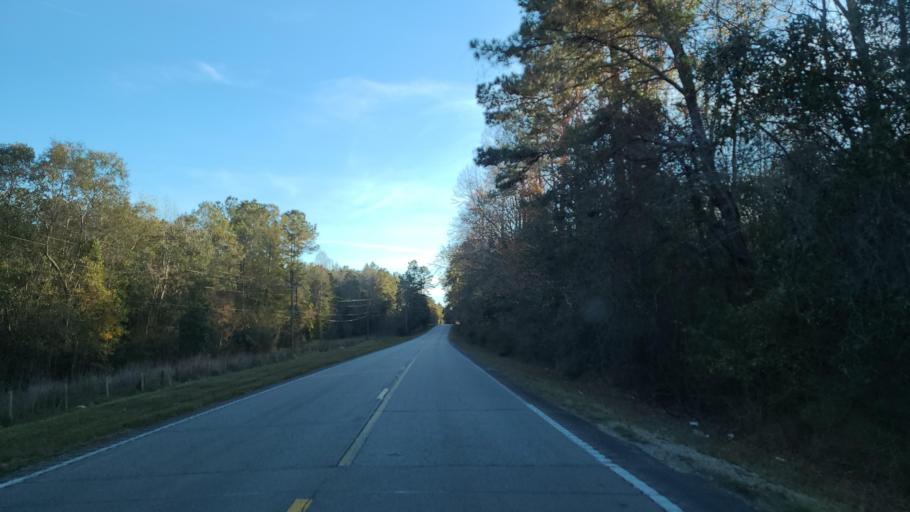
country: US
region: Mississippi
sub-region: Lamar County
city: Purvis
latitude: 31.0815
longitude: -89.4176
